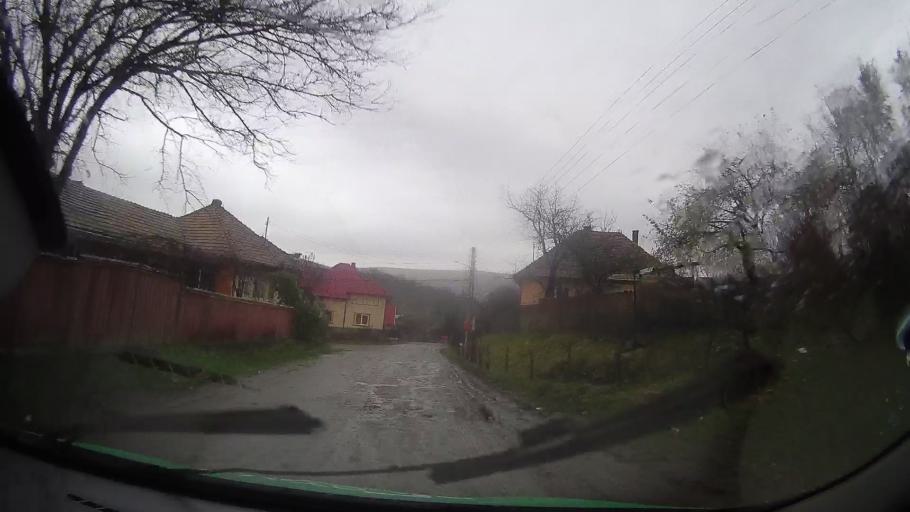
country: RO
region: Bistrita-Nasaud
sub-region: Comuna Monor
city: Monor
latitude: 46.9504
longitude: 24.7048
